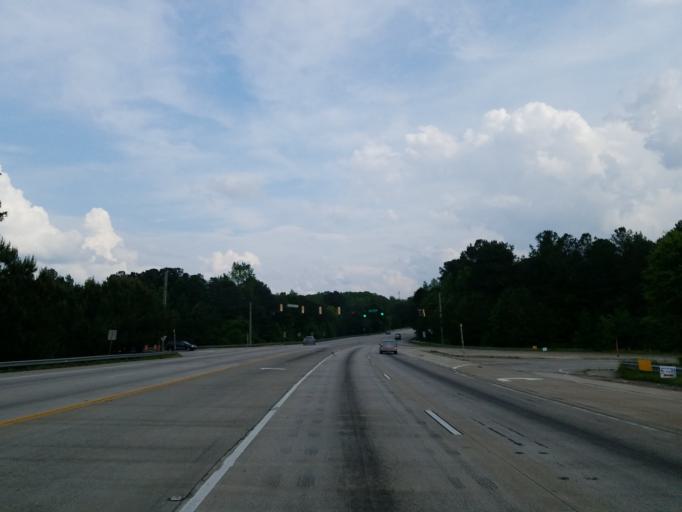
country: US
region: Georgia
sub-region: Cobb County
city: Austell
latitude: 33.8197
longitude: -84.6575
